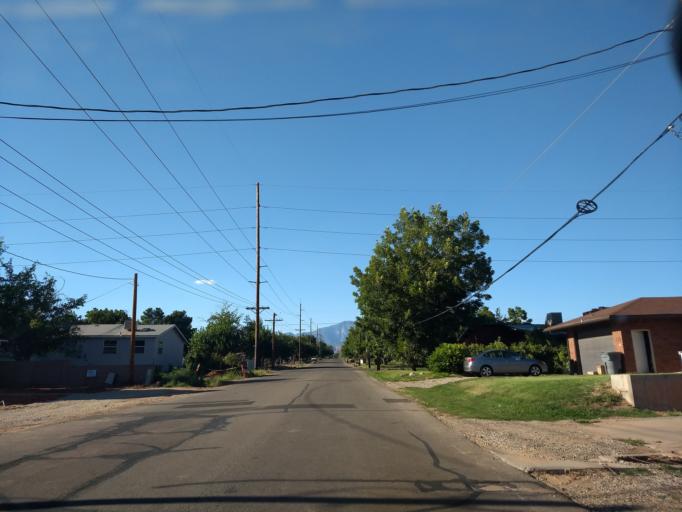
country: US
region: Utah
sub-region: Washington County
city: Washington
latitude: 37.1244
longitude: -113.5082
